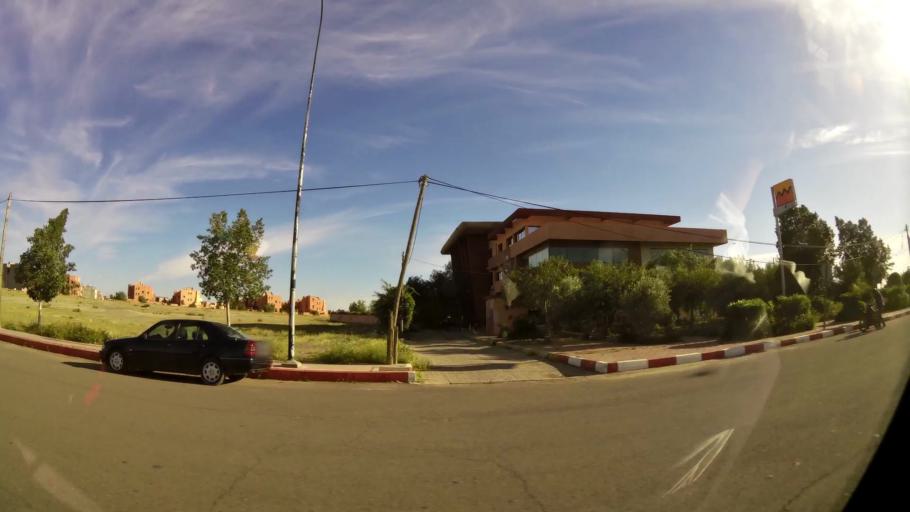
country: MA
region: Marrakech-Tensift-Al Haouz
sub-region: Marrakech
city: Marrakesh
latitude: 31.7541
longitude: -8.1094
